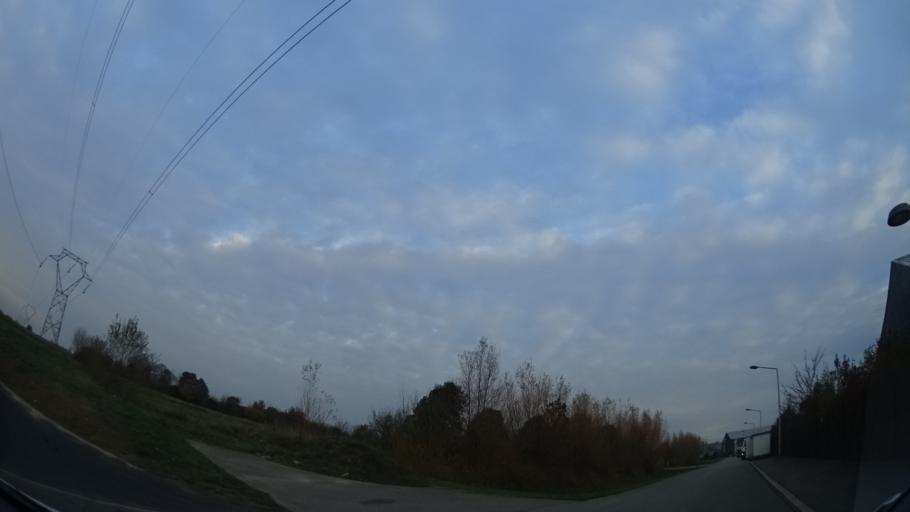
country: FR
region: Brittany
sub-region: Departement d'Ille-et-Vilaine
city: La Chapelle-des-Fougeretz
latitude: 48.1896
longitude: -1.7330
